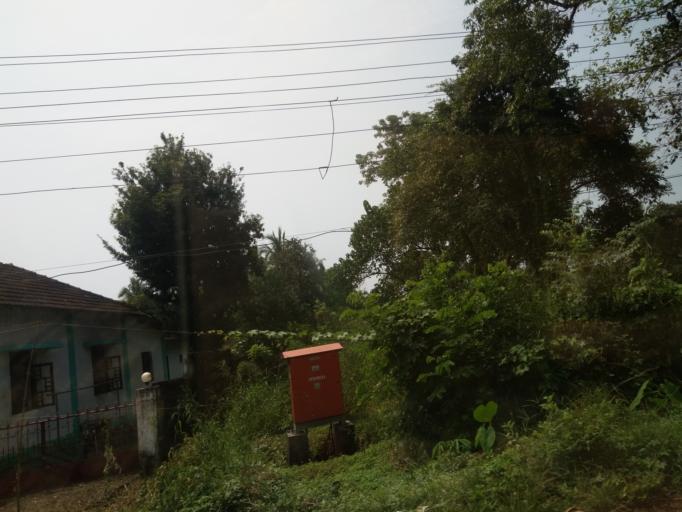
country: IN
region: Goa
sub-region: South Goa
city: Raia
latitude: 15.3218
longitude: 73.9405
